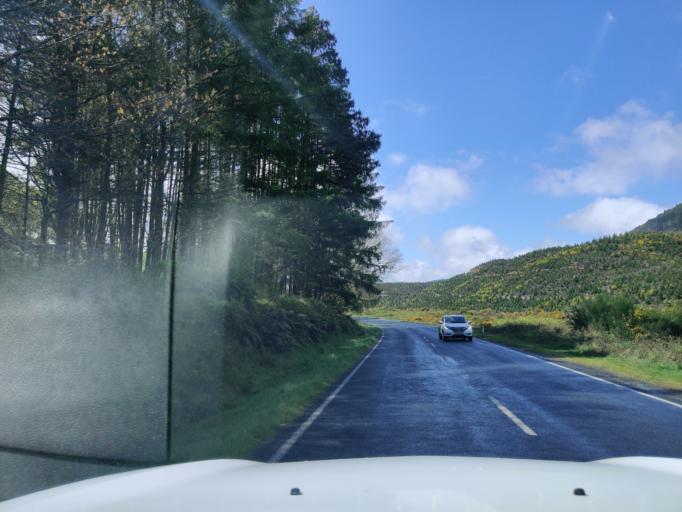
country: NZ
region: Bay of Plenty
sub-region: Rotorua District
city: Rotorua
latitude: -38.1653
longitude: 176.3092
